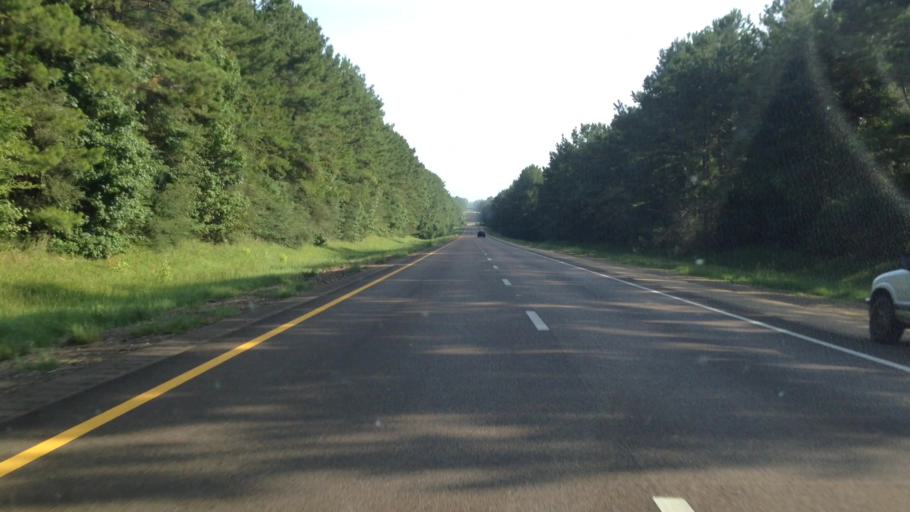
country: US
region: Mississippi
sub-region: Pike County
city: Summit
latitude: 31.3716
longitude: -90.4792
